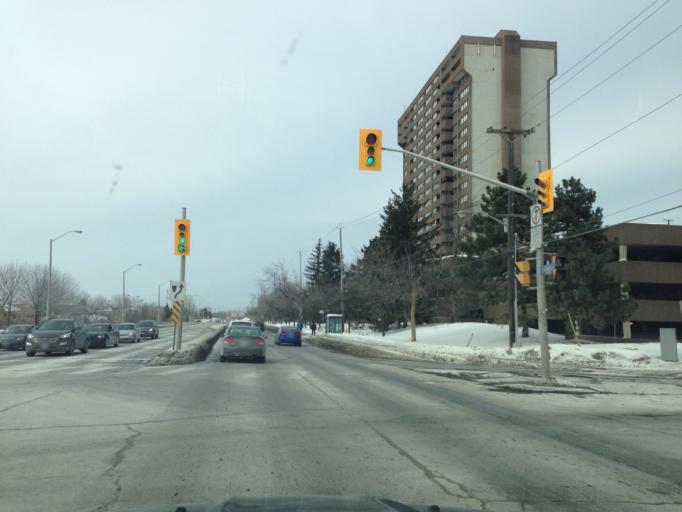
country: CA
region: Ontario
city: Ottawa
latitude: 45.3555
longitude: -75.6509
